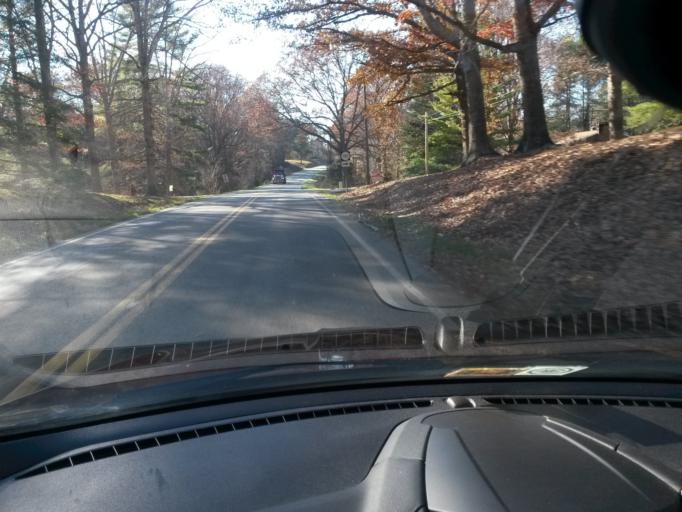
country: US
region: Virginia
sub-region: Charlotte County
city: Charlotte Court House
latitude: 37.0571
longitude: -78.6250
